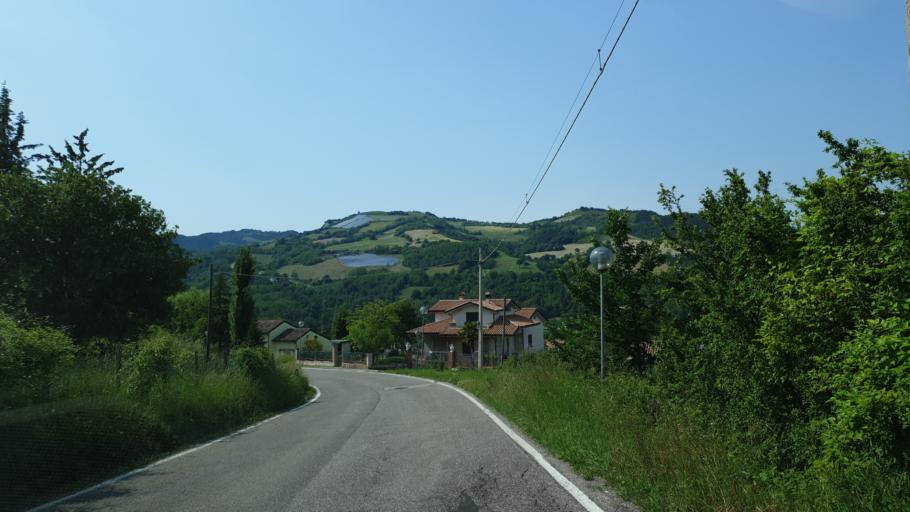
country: IT
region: Emilia-Romagna
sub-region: Forli-Cesena
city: Sarsina
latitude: 43.9184
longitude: 12.1695
